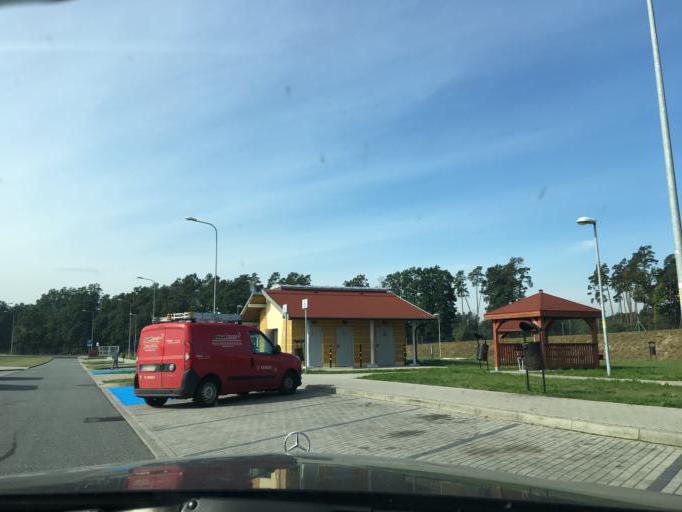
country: PL
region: Lower Silesian Voivodeship
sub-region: Powiat olesnicki
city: Olesnica
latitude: 51.2411
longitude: 17.4997
